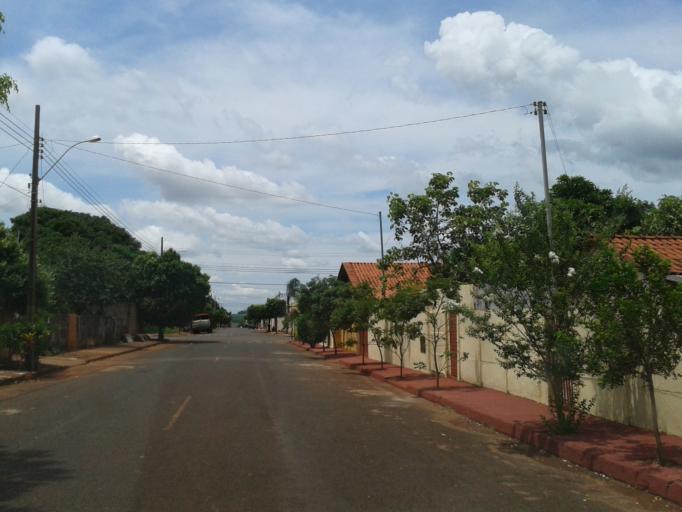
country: BR
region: Minas Gerais
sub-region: Centralina
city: Centralina
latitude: -18.7221
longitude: -49.1984
